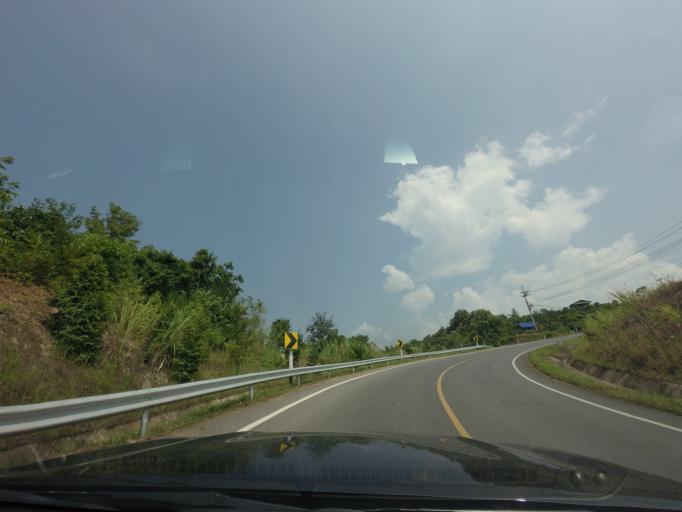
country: TH
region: Nan
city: Santi Suk
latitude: 18.8891
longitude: 100.8354
